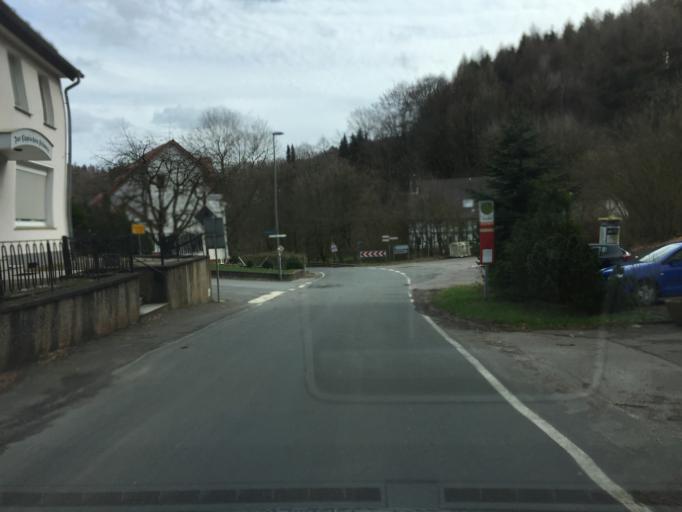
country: DE
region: North Rhine-Westphalia
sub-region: Regierungsbezirk Detmold
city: Detmold
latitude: 51.9003
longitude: 8.8561
